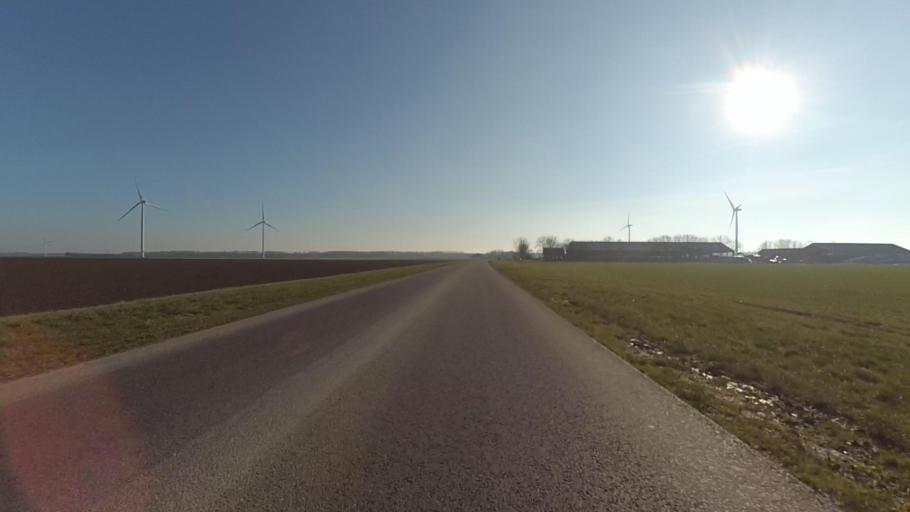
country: NL
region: Utrecht
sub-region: Gemeente Bunschoten
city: Bunschoten
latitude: 52.2846
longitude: 5.4032
